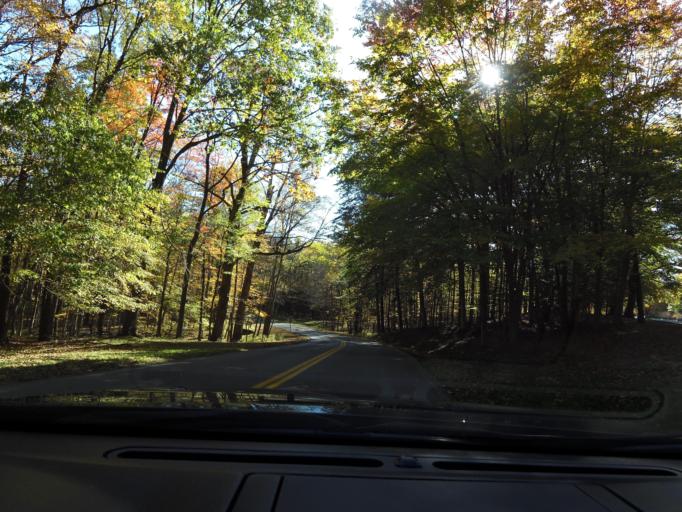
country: US
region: New York
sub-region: Wyoming County
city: Castile
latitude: 42.5933
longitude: -78.0269
